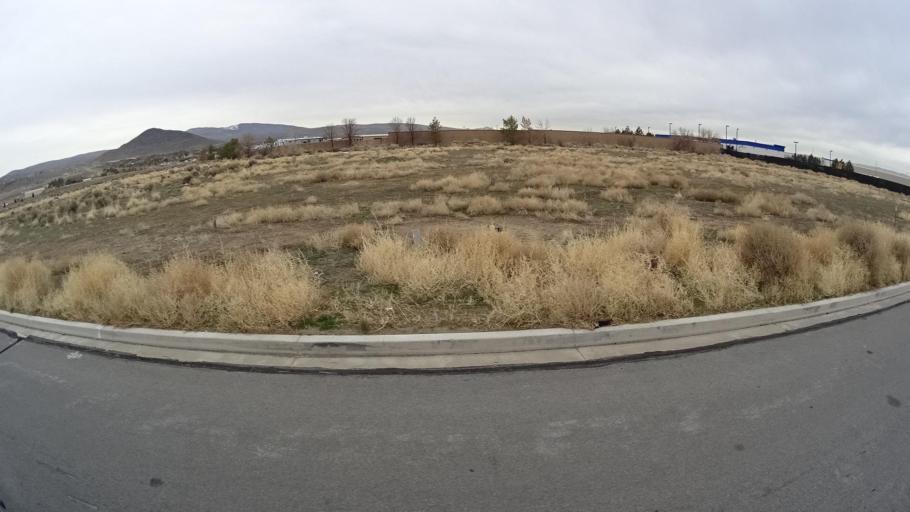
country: US
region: Nevada
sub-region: Washoe County
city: Spanish Springs
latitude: 39.6803
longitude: -119.7040
